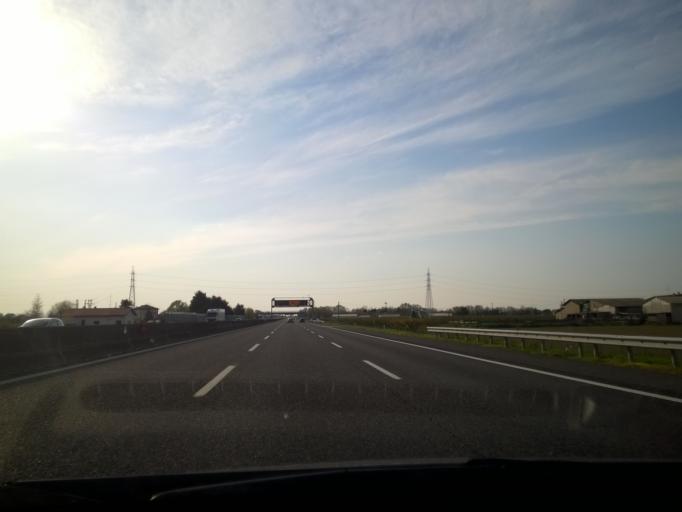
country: IT
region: Emilia-Romagna
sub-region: Forli-Cesena
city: Forli
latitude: 44.2478
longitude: 12.1055
